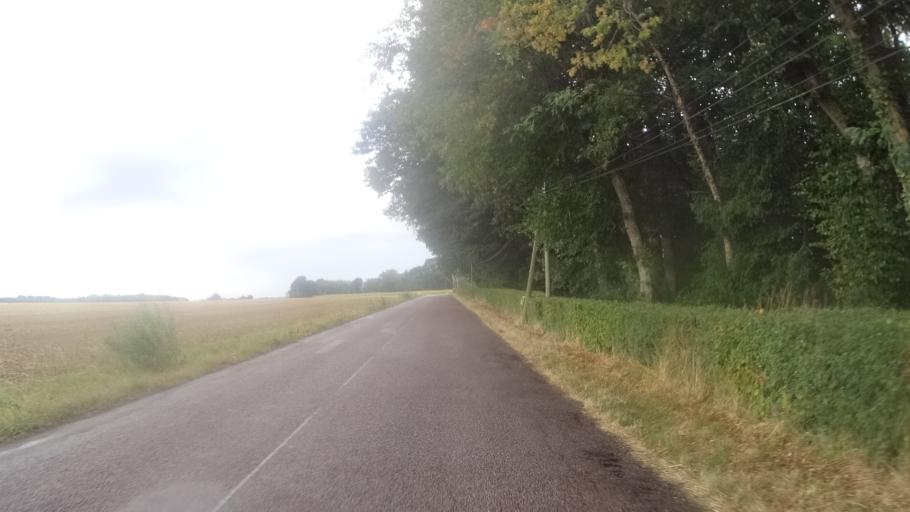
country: FR
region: Bourgogne
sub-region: Departement de Saone-et-Loire
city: Gergy
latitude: 46.9503
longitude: 4.9510
